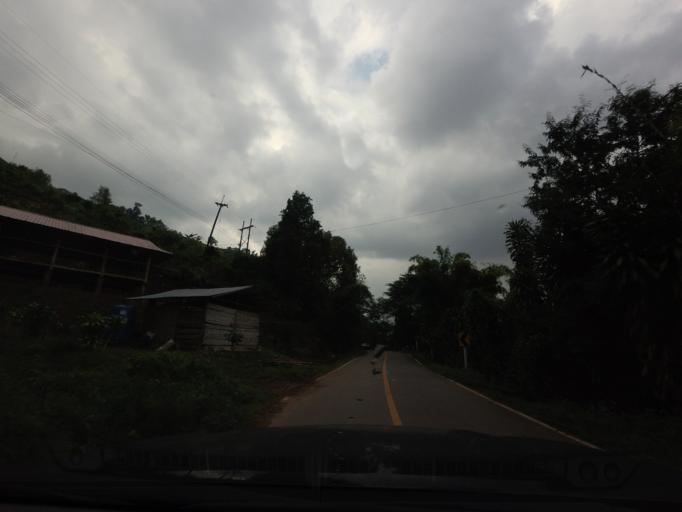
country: TH
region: Nan
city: Bo Kluea
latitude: 19.3189
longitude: 101.1728
